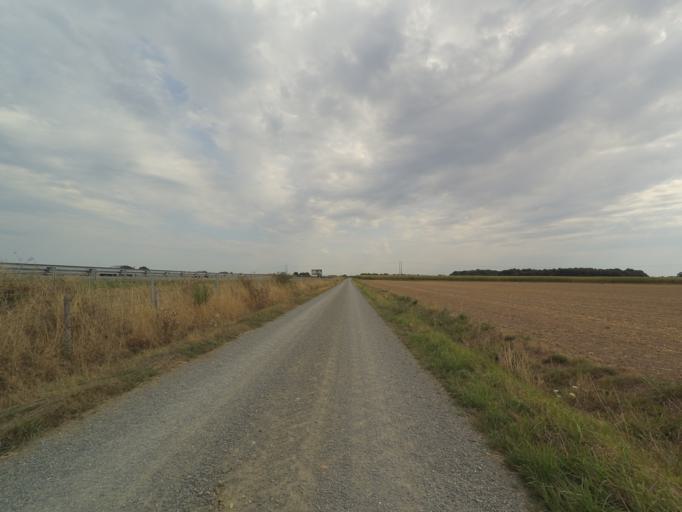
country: FR
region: Pays de la Loire
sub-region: Departement de la Vendee
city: Bouffere
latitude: 46.9786
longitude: -1.3737
